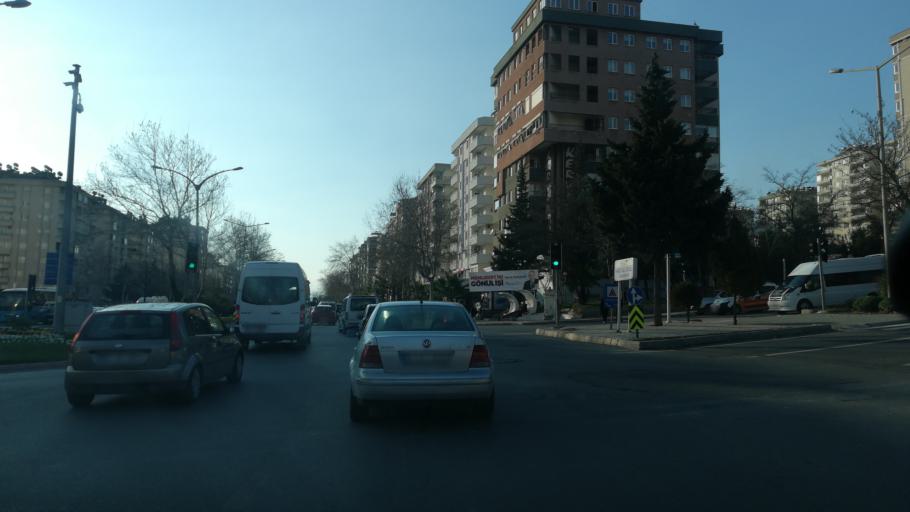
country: TR
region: Kahramanmaras
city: Kahramanmaras
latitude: 37.5885
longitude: 36.8874
